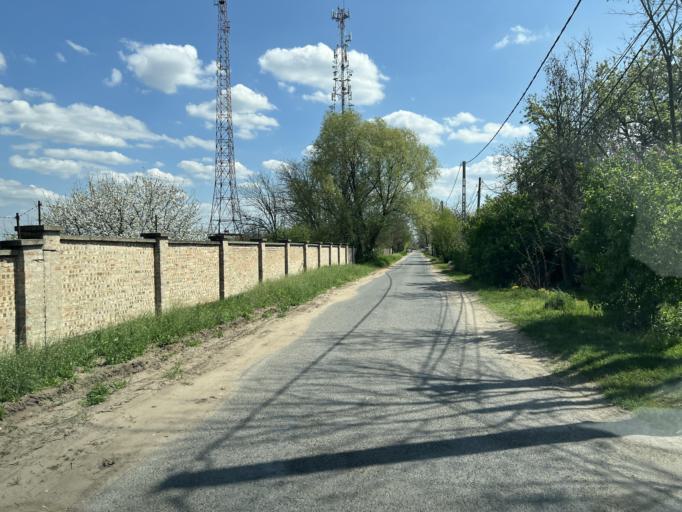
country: HU
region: Pest
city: Gyal
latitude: 47.3859
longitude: 19.2442
